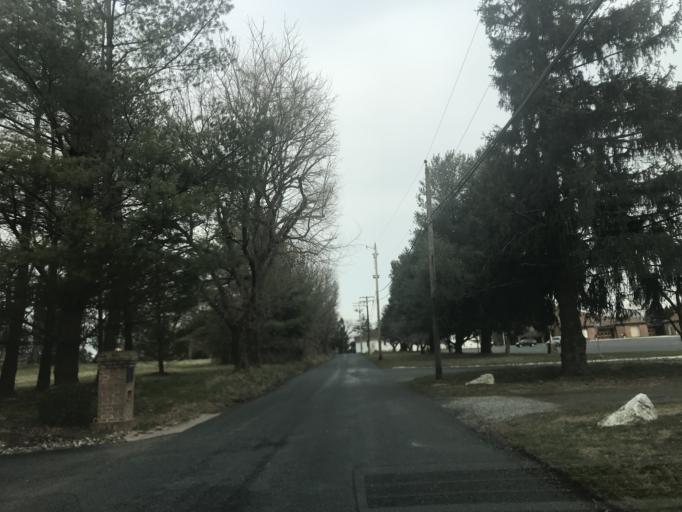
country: US
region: Maryland
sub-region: Harford County
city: Fallston
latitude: 39.5099
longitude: -76.4093
